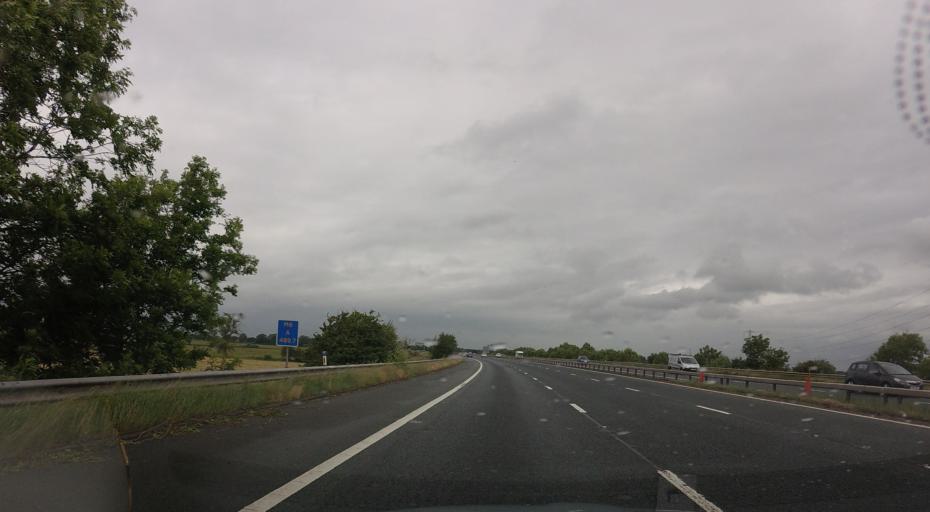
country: GB
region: England
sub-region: Cumbria
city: Scotby
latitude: 54.9045
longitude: -2.8891
